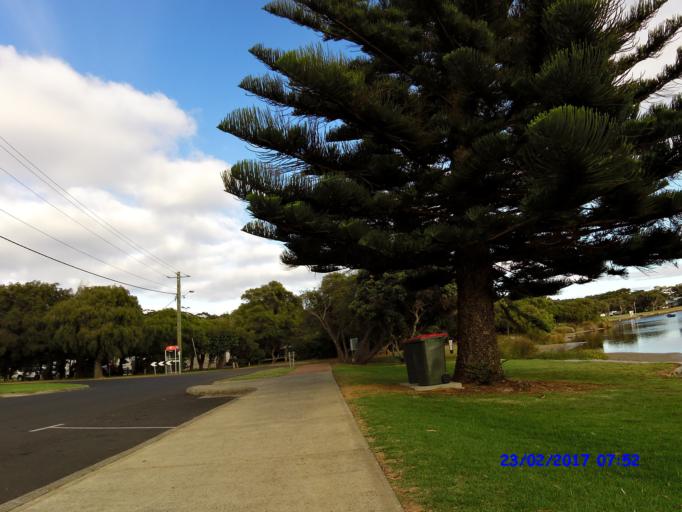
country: AU
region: Western Australia
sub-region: Augusta-Margaret River Shire
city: Augusta
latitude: -34.3246
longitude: 115.1664
